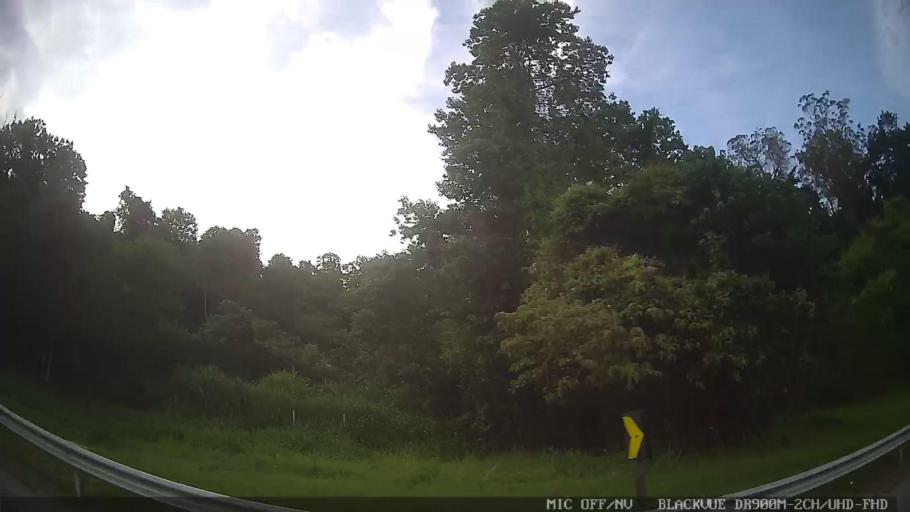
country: BR
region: Sao Paulo
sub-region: Porto Feliz
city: Porto Feliz
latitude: -23.2203
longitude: -47.5724
